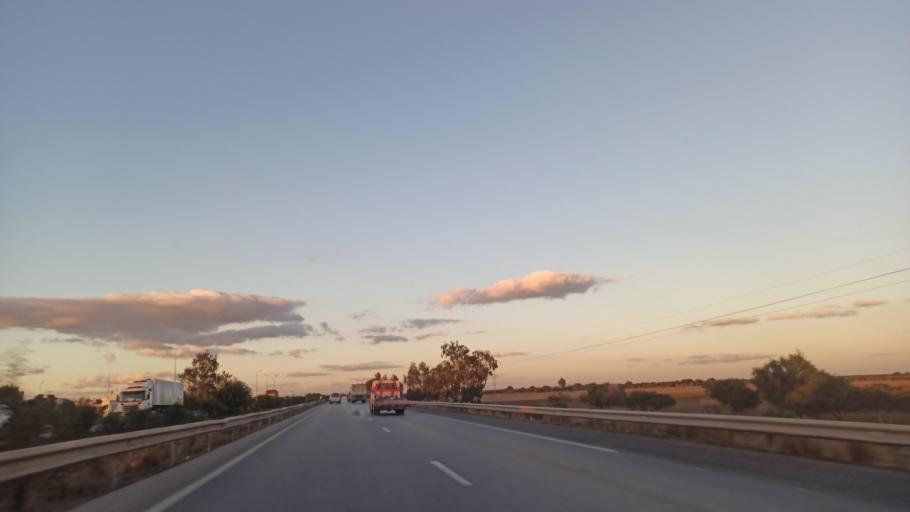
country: TN
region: Susah
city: Harqalah
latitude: 36.1284
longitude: 10.4066
